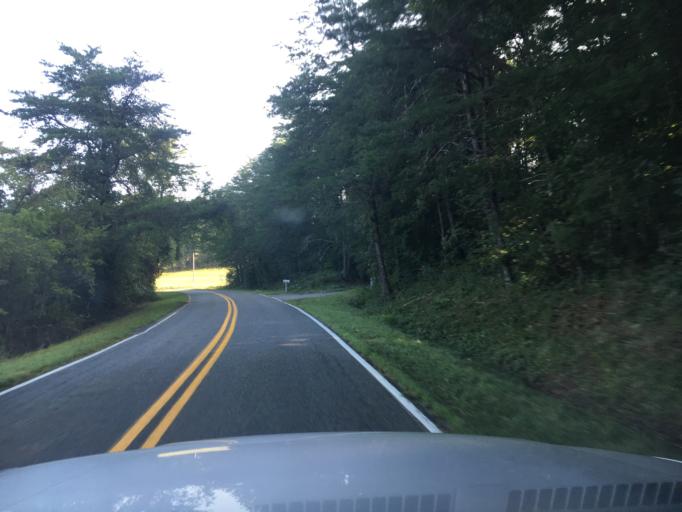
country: US
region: North Carolina
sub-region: Rutherford County
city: Rutherfordton
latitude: 35.2573
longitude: -82.0313
